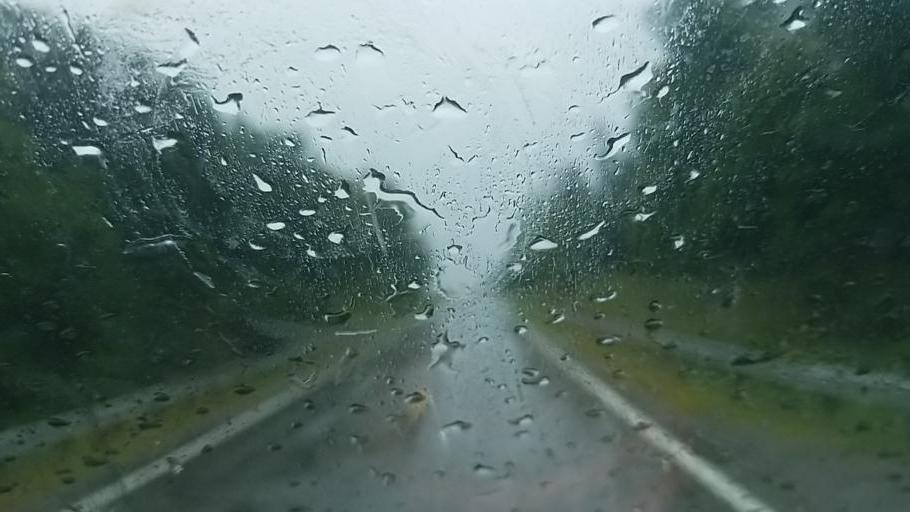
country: US
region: Ohio
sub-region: Champaign County
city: North Lewisburg
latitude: 40.3280
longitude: -83.5957
